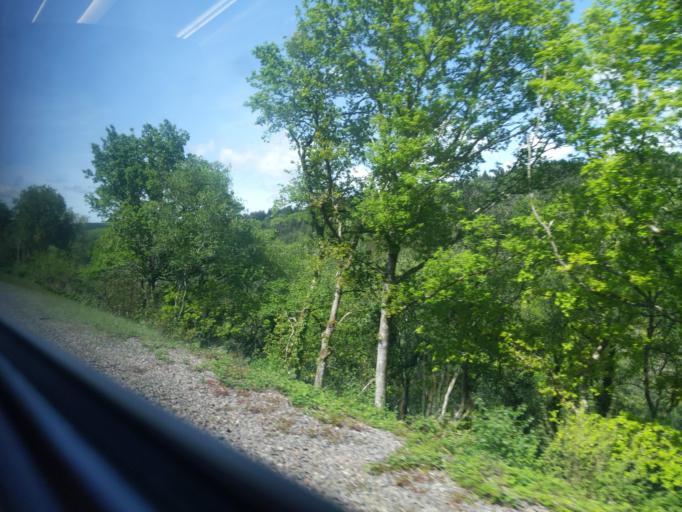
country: GB
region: England
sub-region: Cornwall
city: Lostwithiel
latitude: 50.4533
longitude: -4.5814
